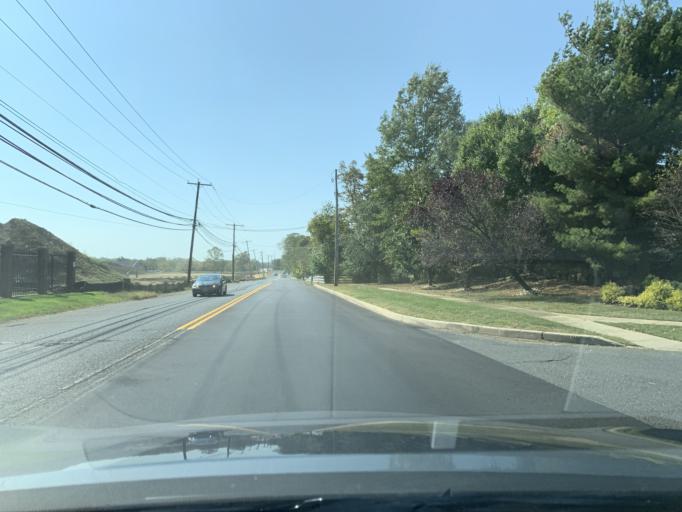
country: US
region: New Jersey
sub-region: Monmouth County
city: Tinton Falls
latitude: 40.3016
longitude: -74.0854
